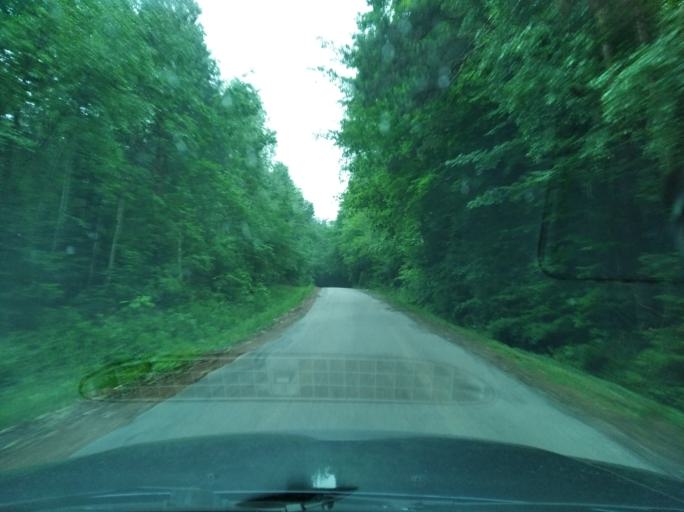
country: PL
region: Subcarpathian Voivodeship
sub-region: Powiat brzozowski
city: Orzechowka
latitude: 49.7264
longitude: 21.9182
